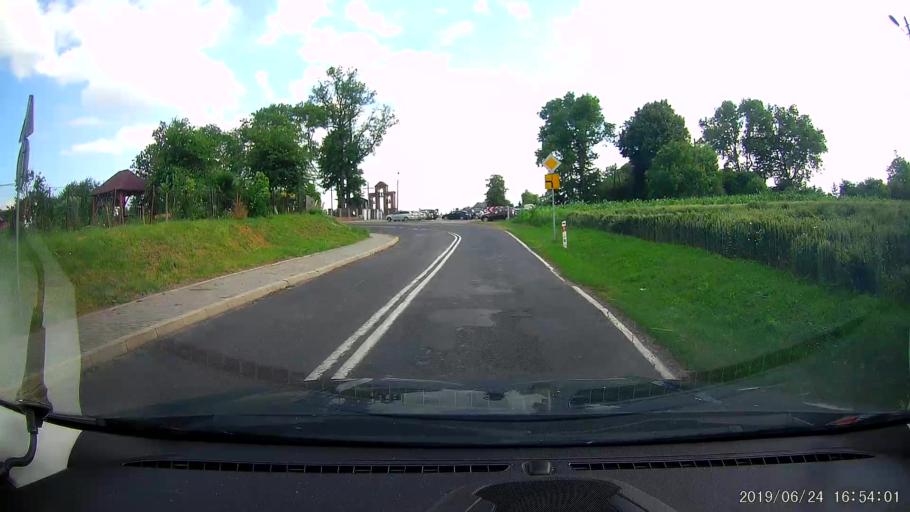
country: PL
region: Lublin Voivodeship
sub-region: Powiat tomaszowski
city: Telatyn
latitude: 50.5333
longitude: 23.8084
